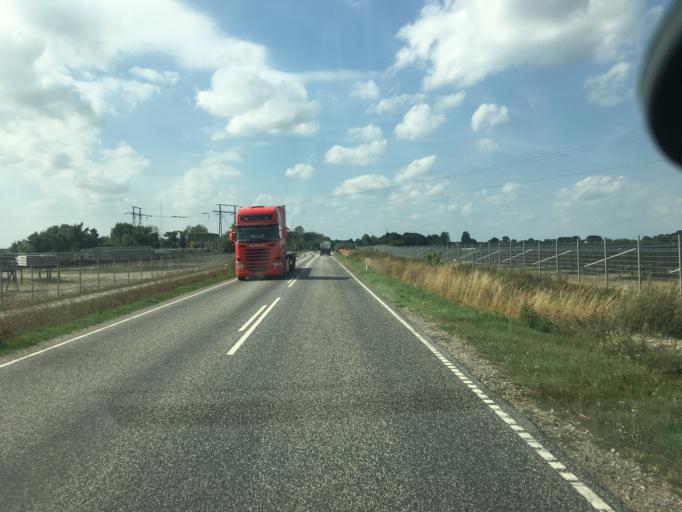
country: DK
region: South Denmark
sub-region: Aabenraa Kommune
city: Tinglev
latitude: 54.9431
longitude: 9.2680
